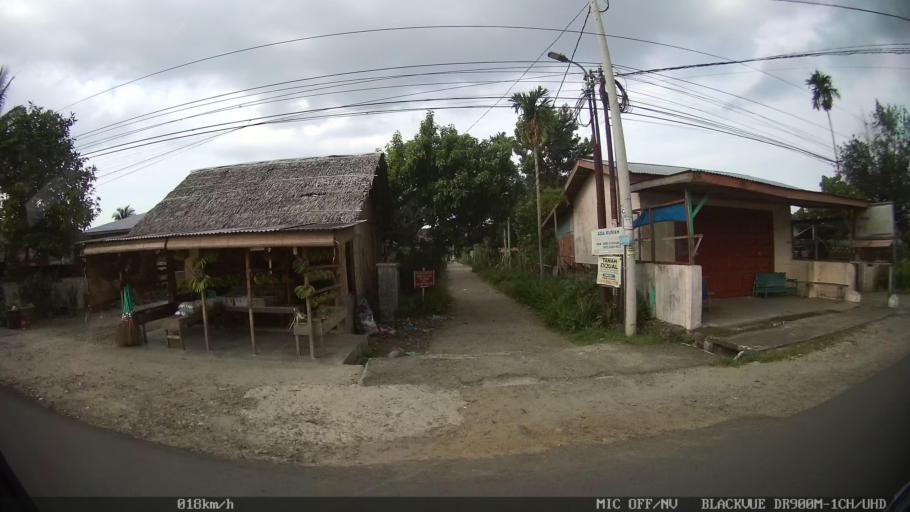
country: ID
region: North Sumatra
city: Sunggal
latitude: 3.5254
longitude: 98.6129
